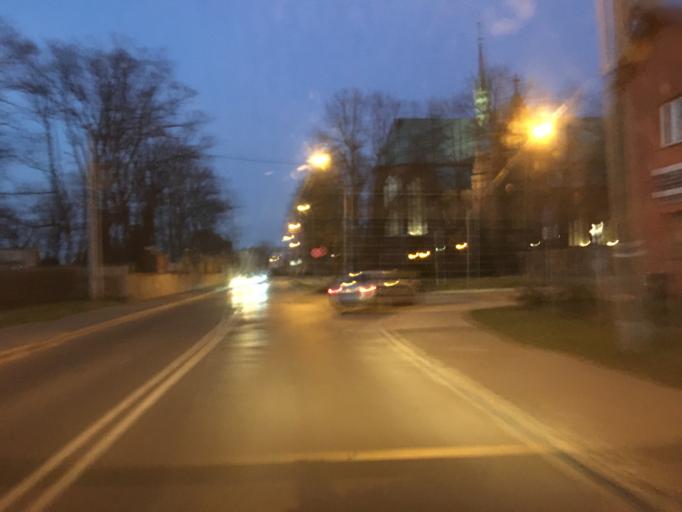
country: PL
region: Lower Silesian Voivodeship
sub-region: Powiat dzierzoniowski
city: Bielawa
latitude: 50.6867
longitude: 16.6148
